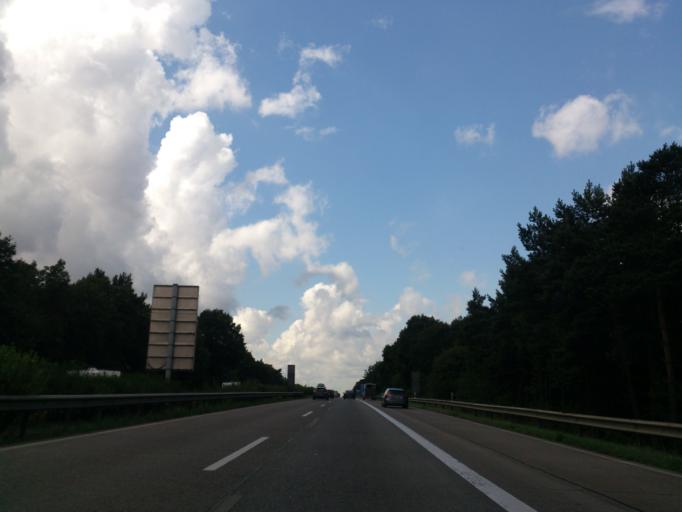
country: DE
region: Lower Saxony
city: Soltau
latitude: 52.9539
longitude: 9.8846
